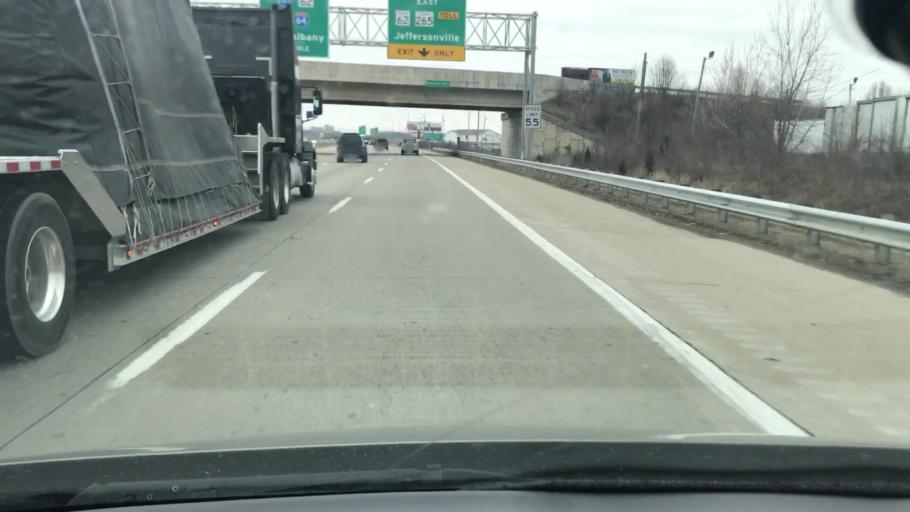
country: US
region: Indiana
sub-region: Clark County
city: Clarksville
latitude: 38.3355
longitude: -85.7533
